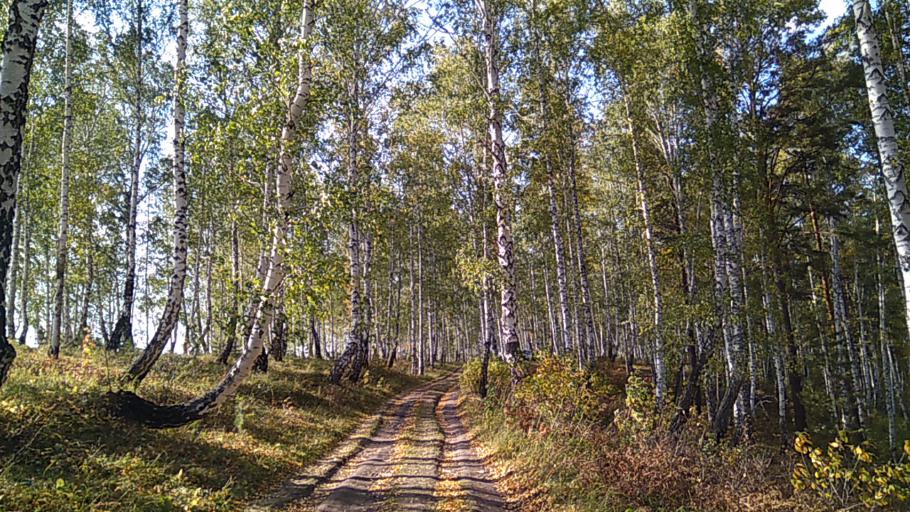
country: RU
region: Sverdlovsk
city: Pokrovskoye
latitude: 56.4281
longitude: 61.6124
